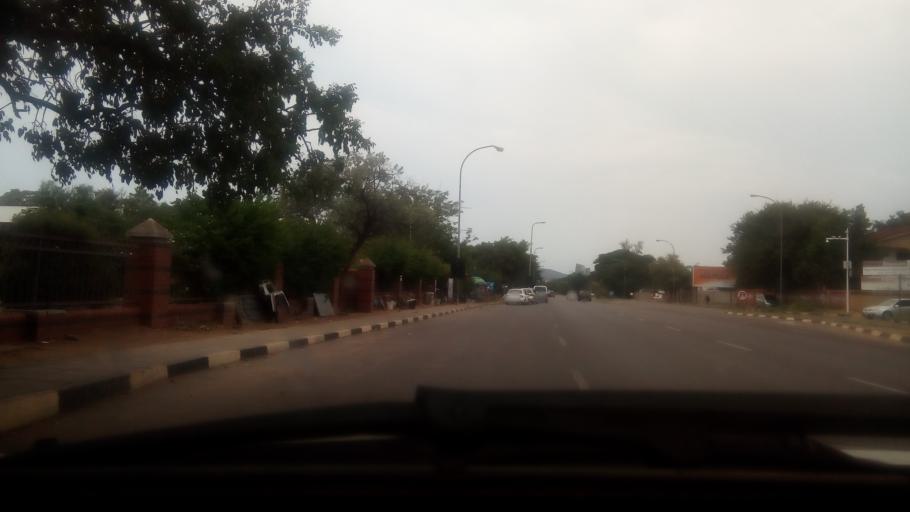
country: BW
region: South East
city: Gaborone
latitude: -24.6618
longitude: 25.9293
